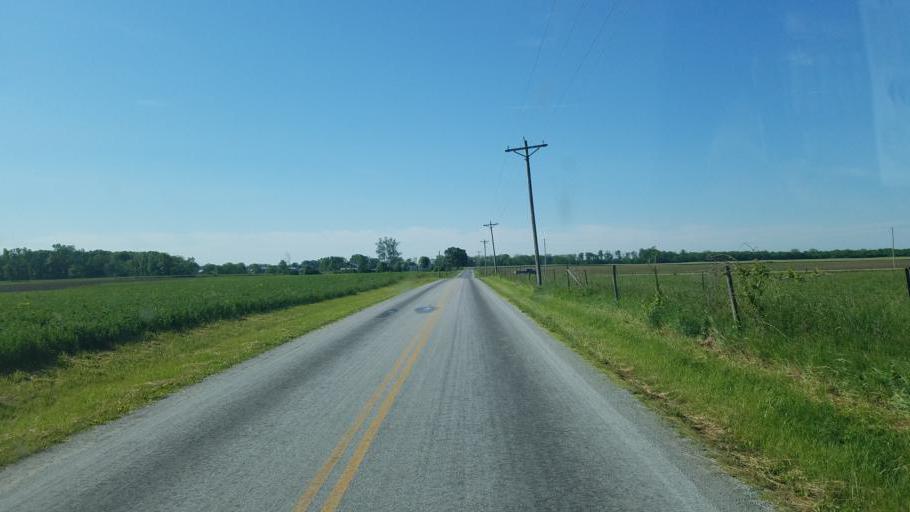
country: US
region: Ohio
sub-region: Hardin County
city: Kenton
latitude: 40.5727
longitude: -83.4526
